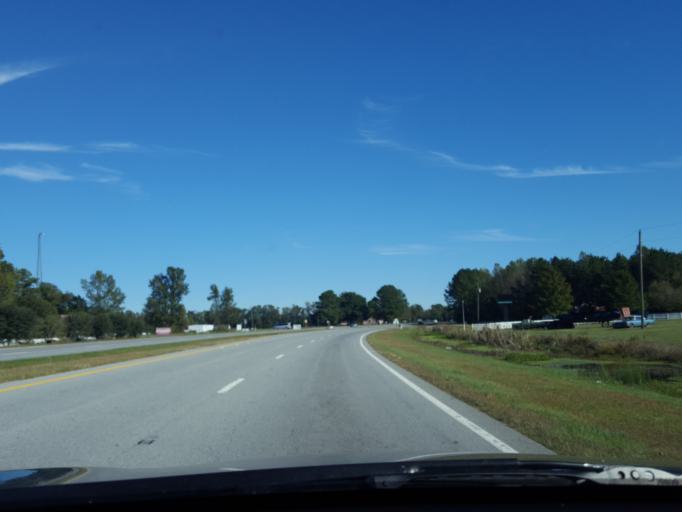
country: US
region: North Carolina
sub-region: Beaufort County
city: Washington
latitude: 35.6250
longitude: -77.1812
